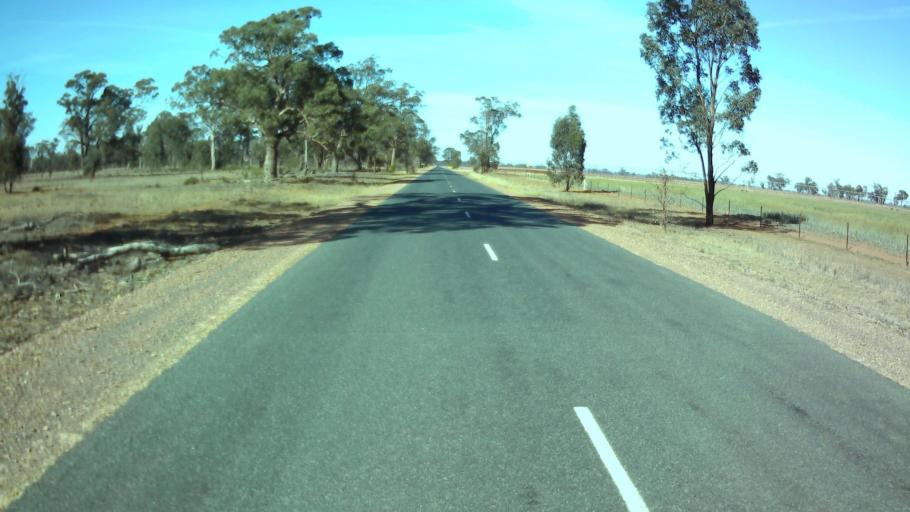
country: AU
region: New South Wales
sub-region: Weddin
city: Grenfell
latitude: -34.1161
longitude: 147.8189
